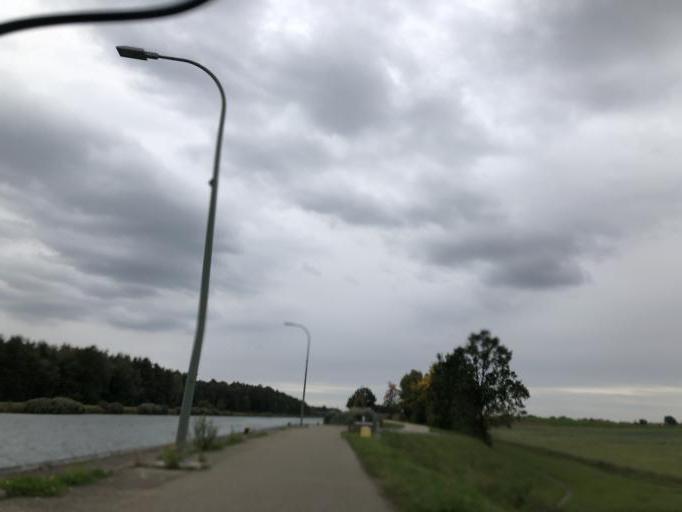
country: DE
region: Bavaria
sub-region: Regierungsbezirk Mittelfranken
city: Erlangen
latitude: 49.5517
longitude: 10.9688
